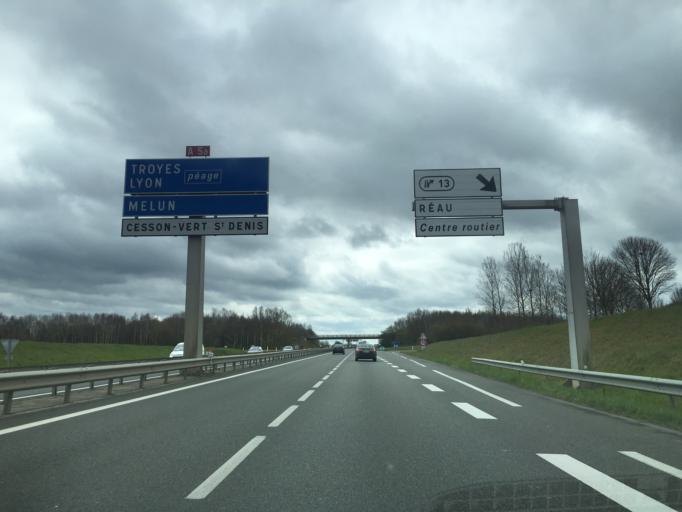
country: FR
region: Ile-de-France
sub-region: Departement de Seine-et-Marne
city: Moissy-Cramayel
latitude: 48.6167
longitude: 2.6310
